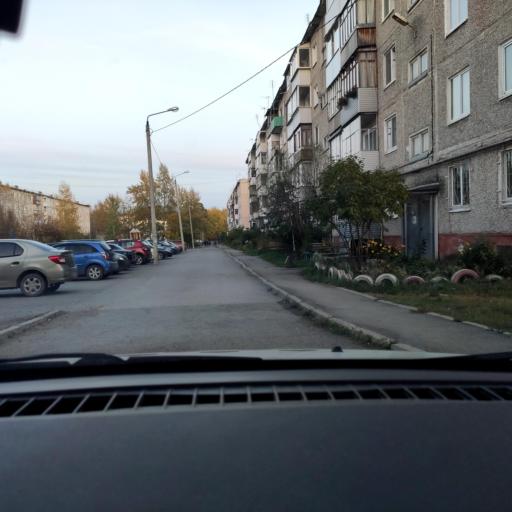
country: RU
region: Perm
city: Overyata
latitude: 58.0287
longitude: 55.8354
